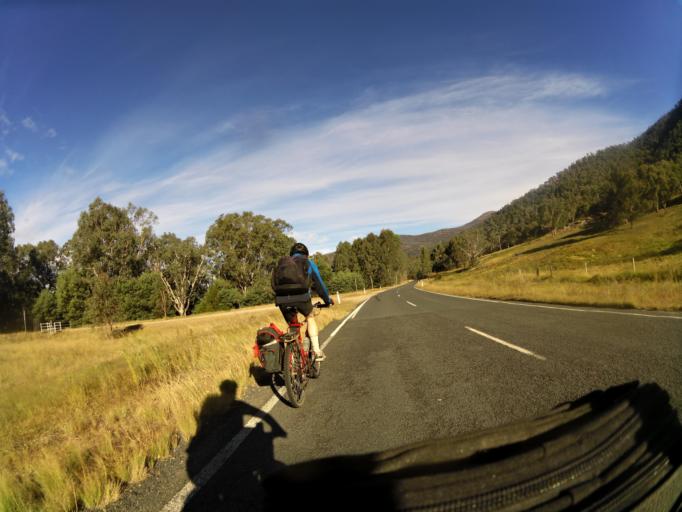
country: AU
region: New South Wales
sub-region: Greater Hume Shire
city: Holbrook
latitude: -35.9755
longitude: 147.8120
